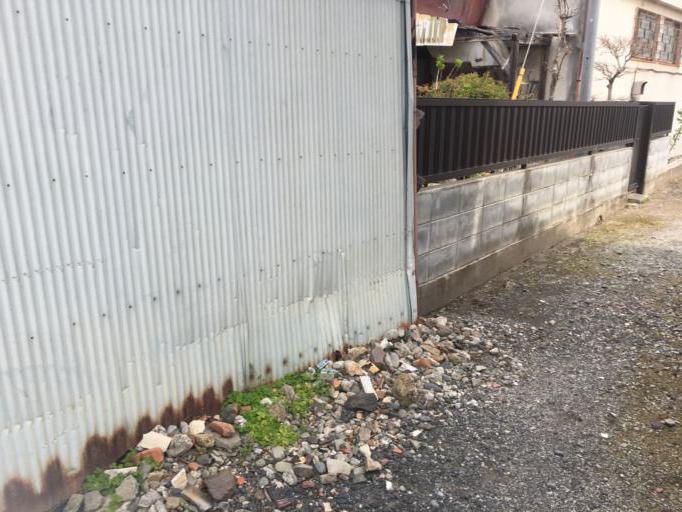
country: JP
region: Saitama
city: Gyoda
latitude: 36.1404
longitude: 139.4606
